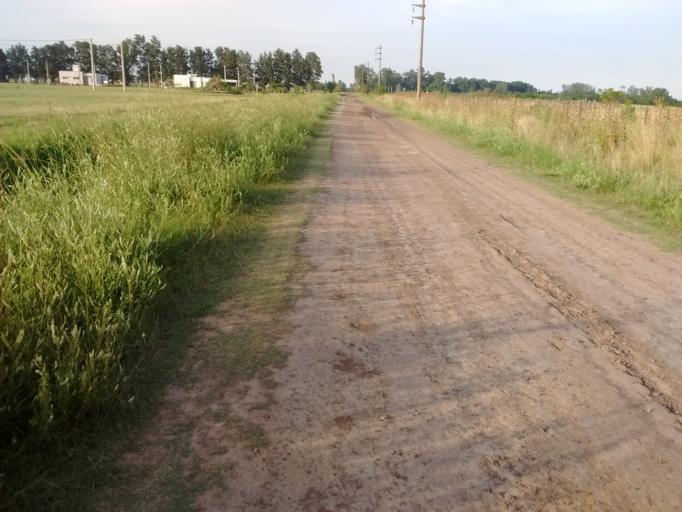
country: AR
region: Santa Fe
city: Roldan
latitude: -32.9294
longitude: -60.8719
